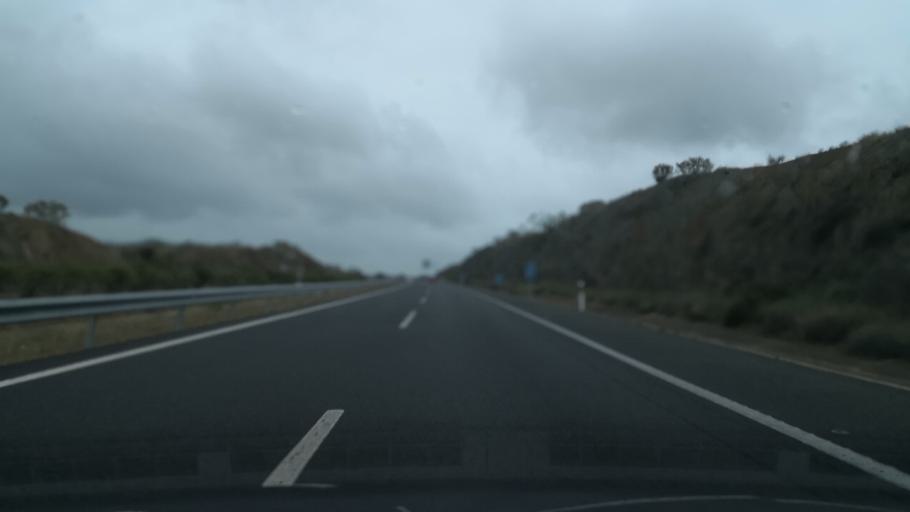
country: ES
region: Extremadura
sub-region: Provincia de Caceres
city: Hinojal
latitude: 39.7053
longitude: -6.4064
